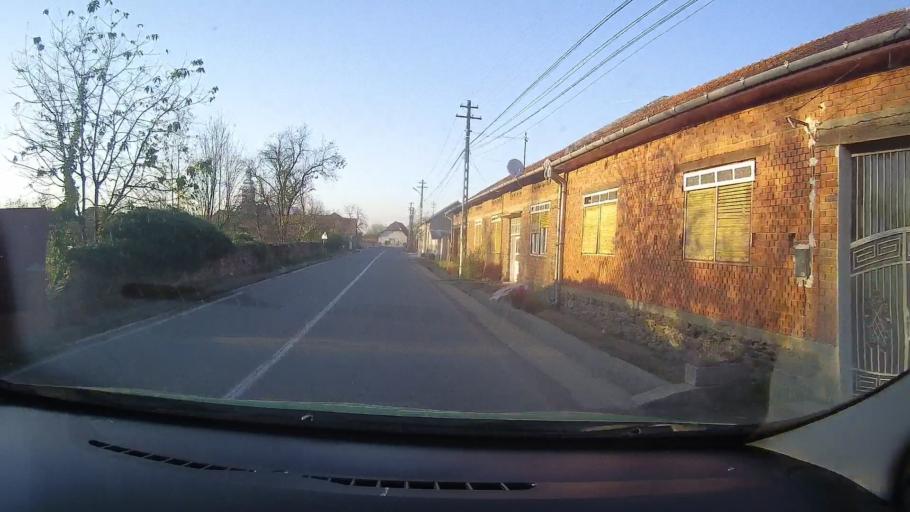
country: RO
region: Timis
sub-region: Comuna Traian Vuia
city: Traian Vuia
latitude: 45.7657
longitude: 22.0953
